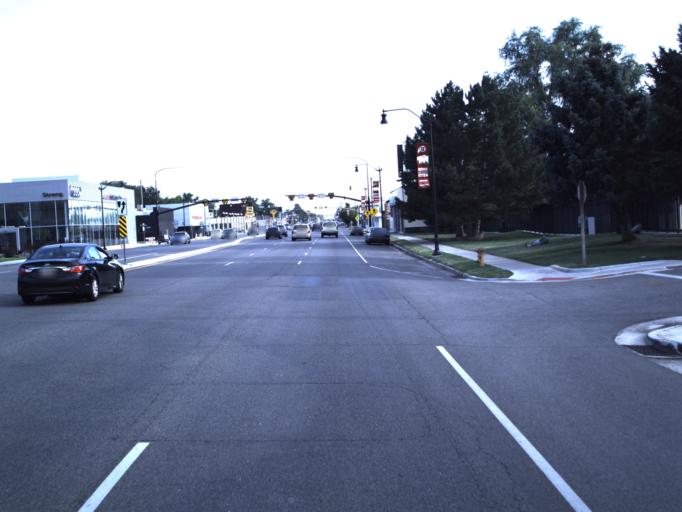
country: US
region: Utah
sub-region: Salt Lake County
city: Salt Lake City
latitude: 40.7482
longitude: -111.8884
